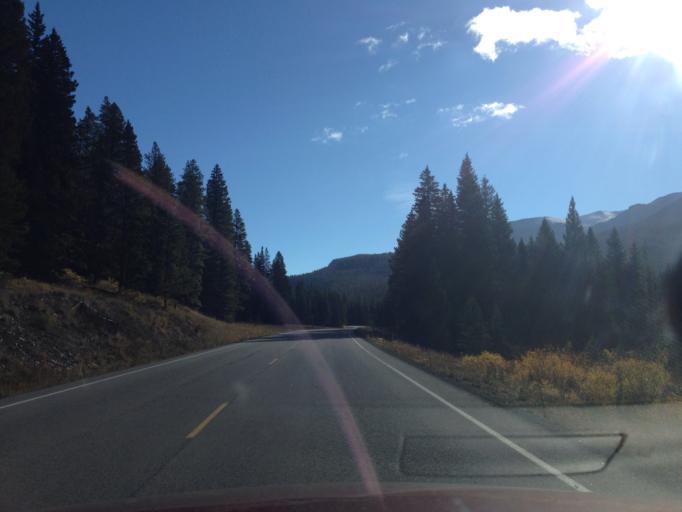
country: US
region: Montana
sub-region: Stillwater County
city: Absarokee
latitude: 45.0183
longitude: -109.9457
